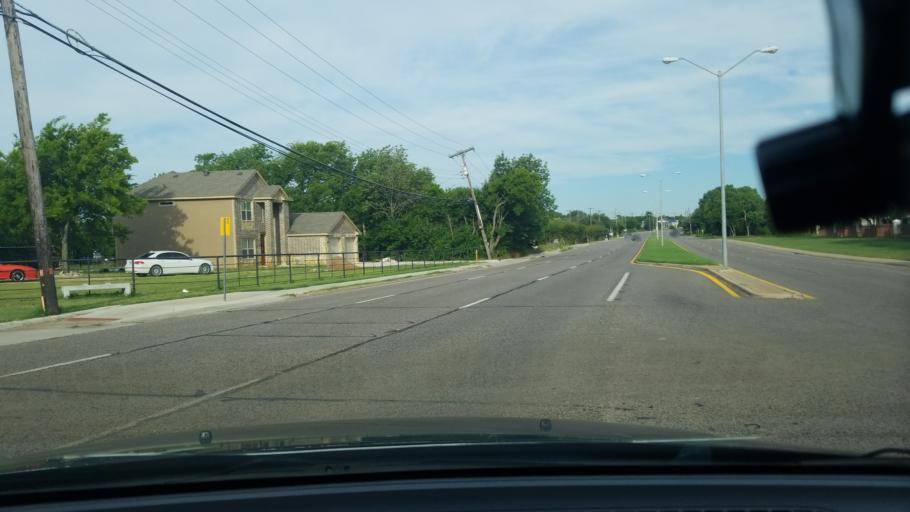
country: US
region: Texas
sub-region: Dallas County
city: Balch Springs
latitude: 32.7623
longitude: -96.6506
